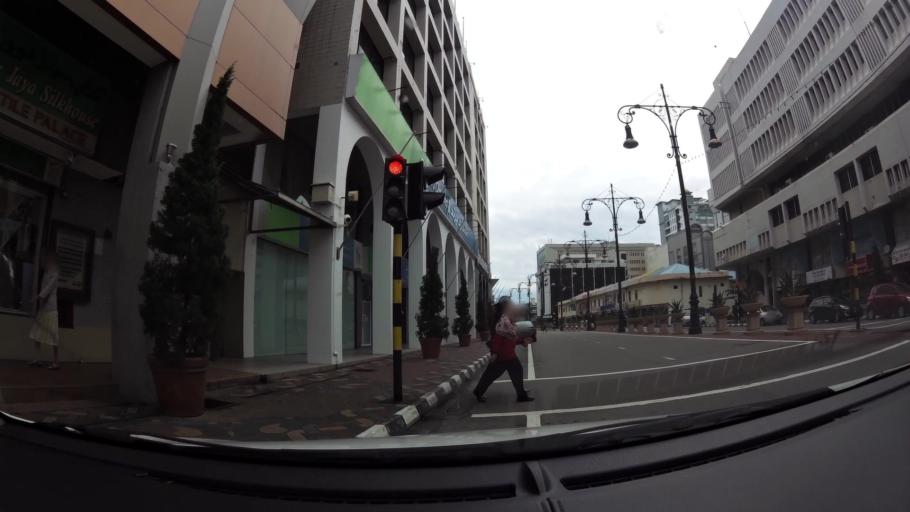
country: BN
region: Brunei and Muara
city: Bandar Seri Begawan
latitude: 4.8875
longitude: 114.9429
